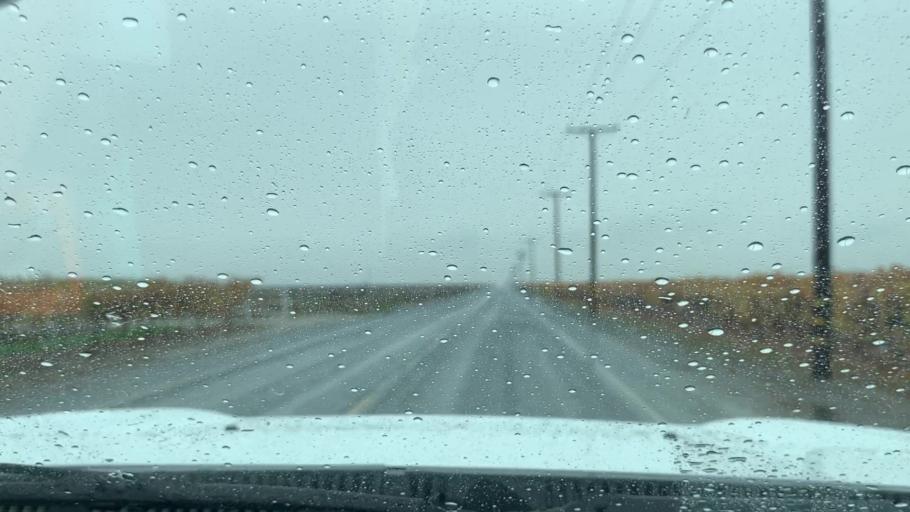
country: US
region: California
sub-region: Tulare County
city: Earlimart
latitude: 35.8919
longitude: -119.2813
